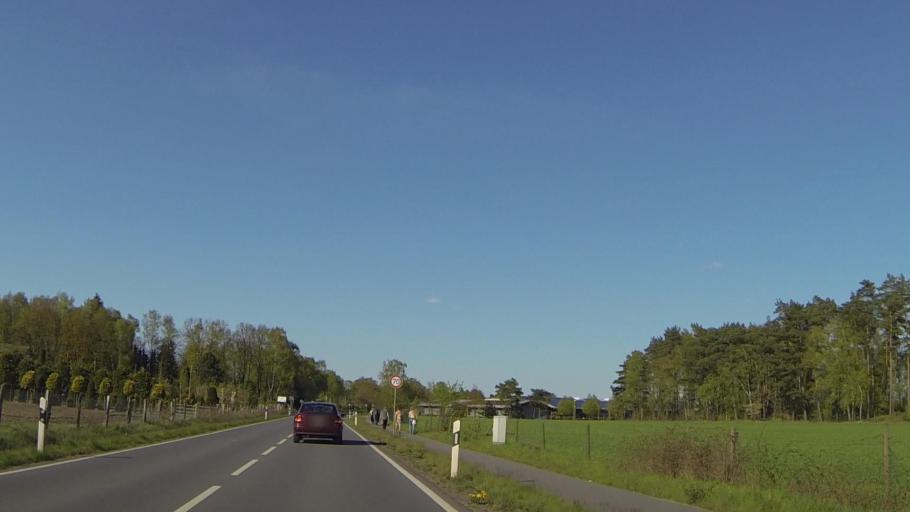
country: DE
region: Schleswig-Holstein
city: Appen
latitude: 53.6237
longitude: 9.7297
